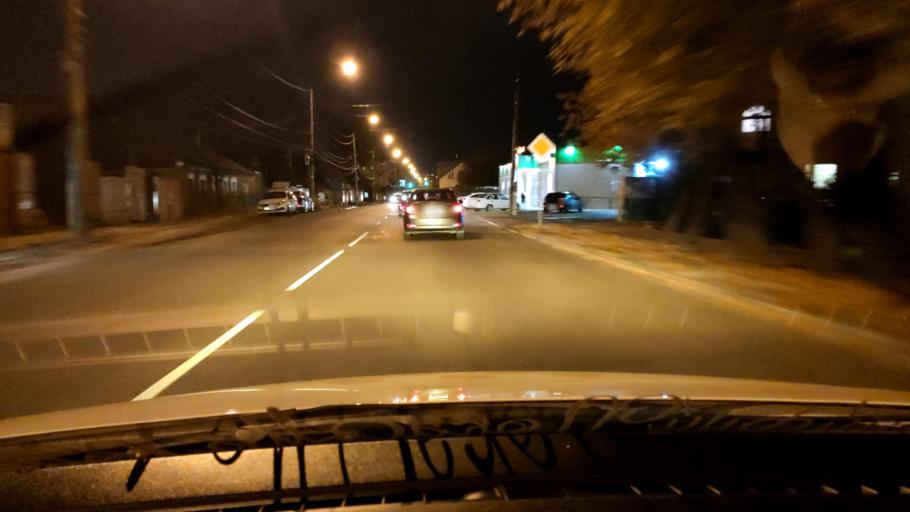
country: RU
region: Voronezj
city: Voronezh
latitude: 51.6858
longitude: 39.2117
